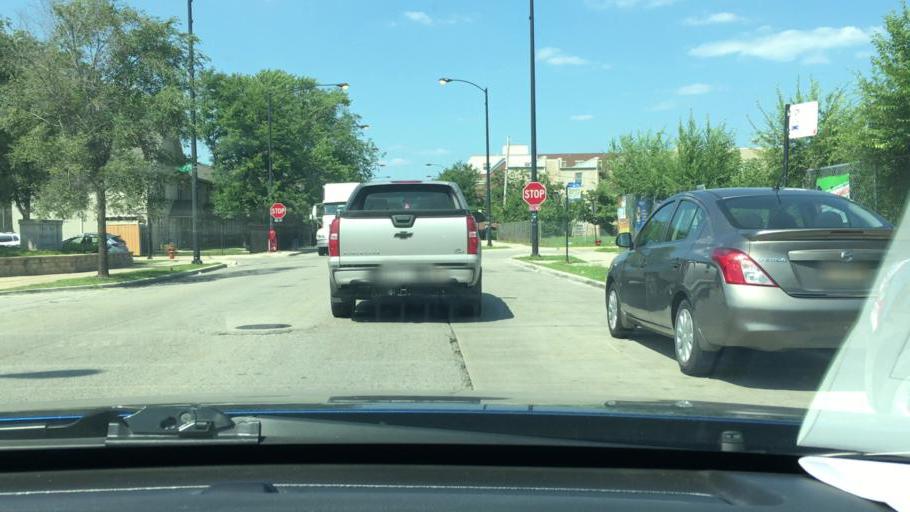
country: US
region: Illinois
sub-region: Cook County
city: Chicago
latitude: 41.8648
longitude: -87.6566
